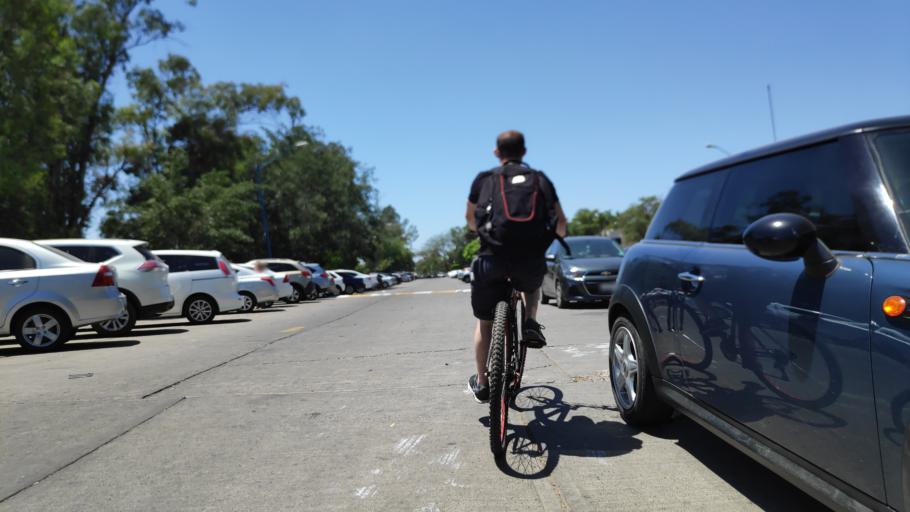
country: MX
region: Sinaloa
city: Culiacan
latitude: 24.8256
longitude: -107.3806
